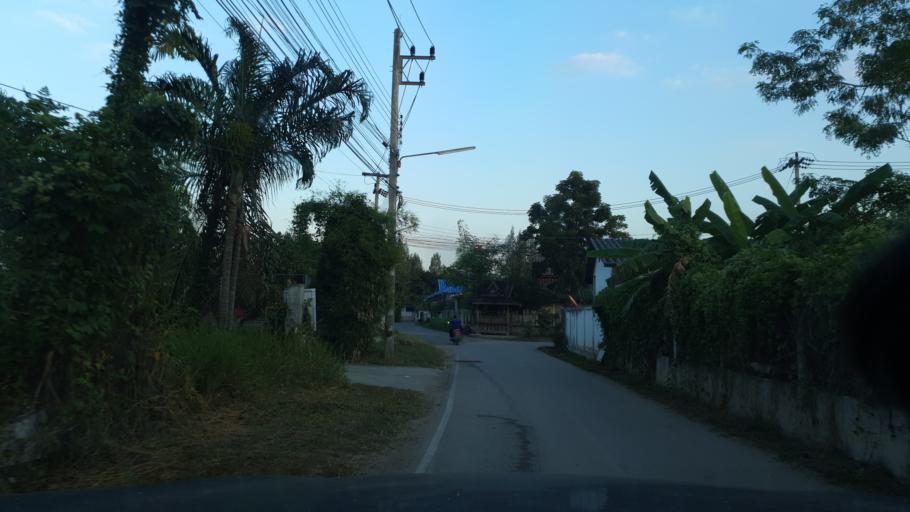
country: TH
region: Chiang Mai
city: San Sai
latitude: 18.8476
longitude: 99.0727
